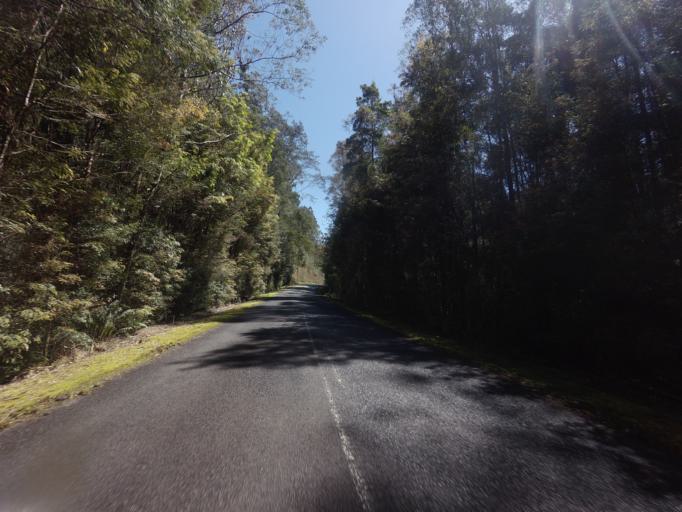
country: AU
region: Tasmania
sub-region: Huon Valley
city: Geeveston
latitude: -42.8223
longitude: 146.3121
